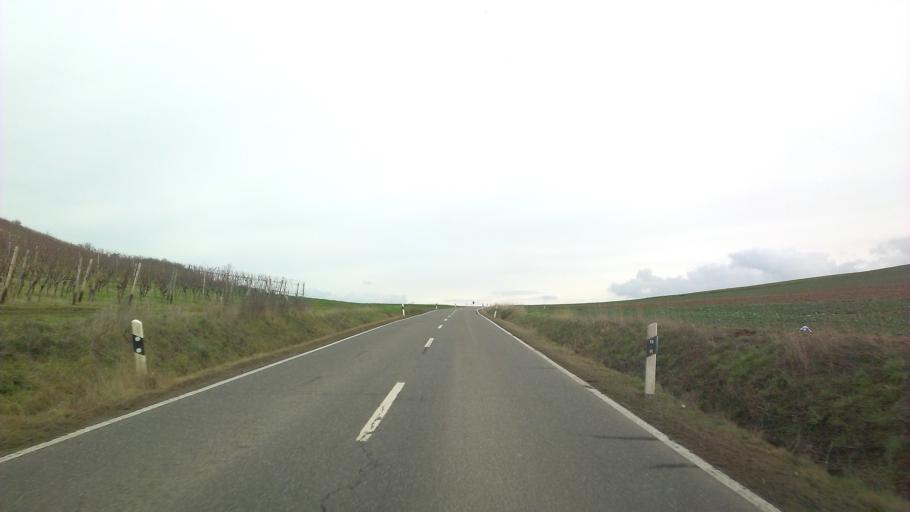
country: DE
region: Rheinland-Pfalz
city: Siefersheim
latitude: 49.7873
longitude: 7.9368
